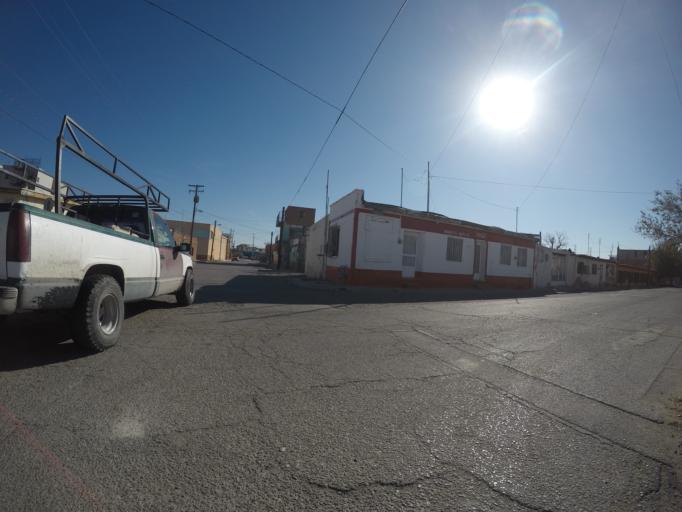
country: MX
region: Chihuahua
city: Ciudad Juarez
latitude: 31.7438
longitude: -106.4827
